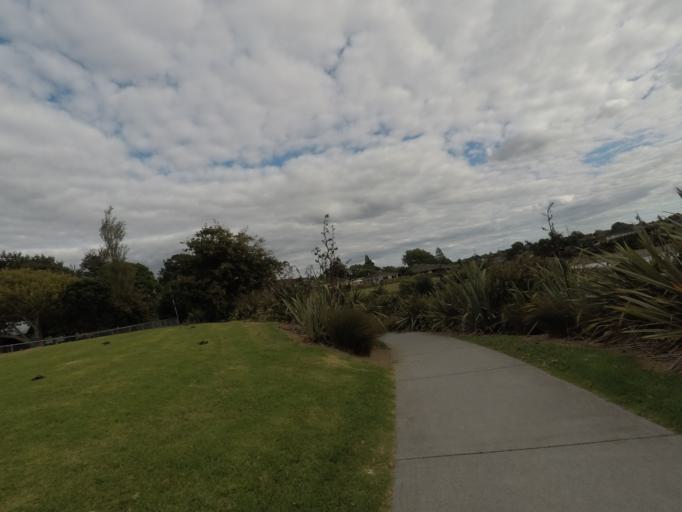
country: NZ
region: Auckland
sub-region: Auckland
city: Papakura
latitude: -37.0622
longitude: 174.9339
